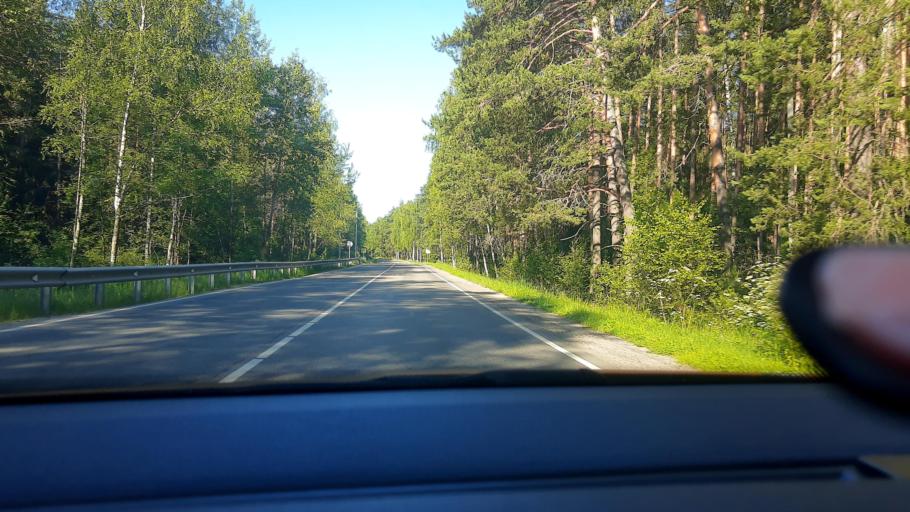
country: RU
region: Moskovskaya
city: Pavlovskiy Posad
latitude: 55.8696
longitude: 38.6851
